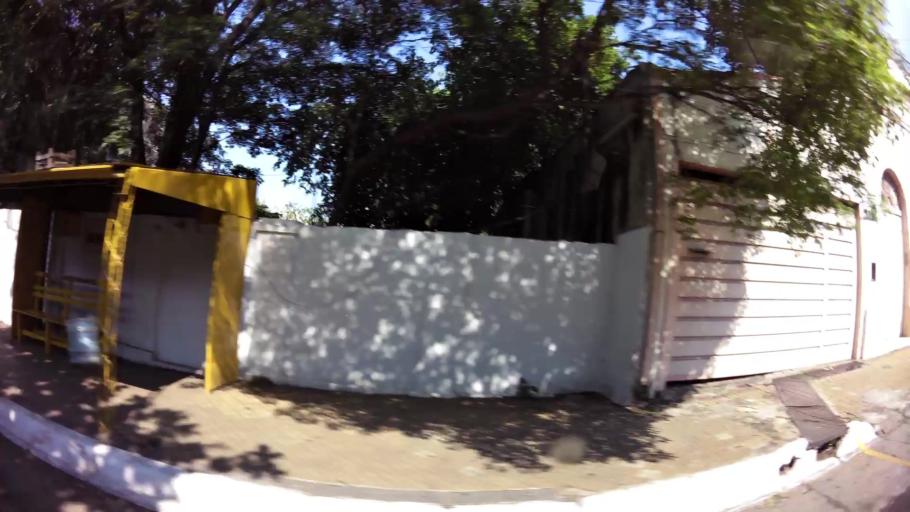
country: PY
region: Asuncion
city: Asuncion
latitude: -25.2933
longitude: -57.6303
